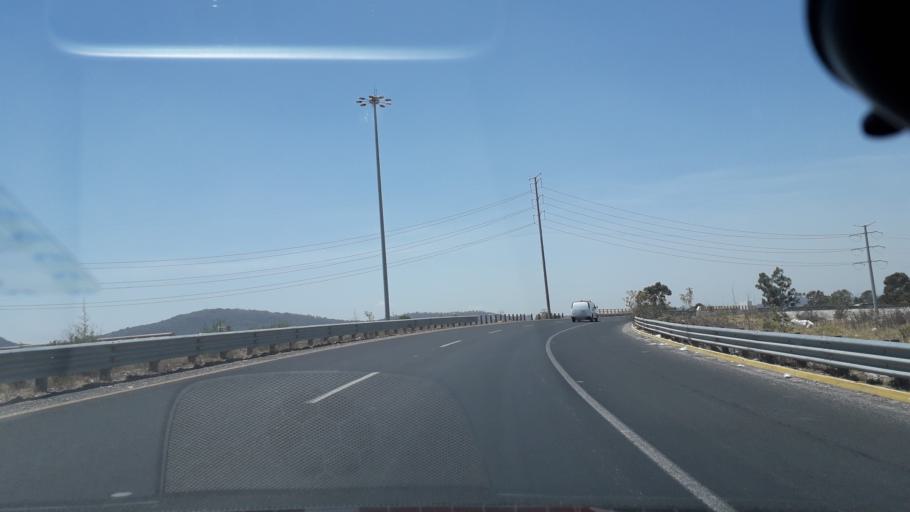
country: MX
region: Puebla
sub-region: Amozoc
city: Casa Blanca
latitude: 19.0611
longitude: -98.1071
